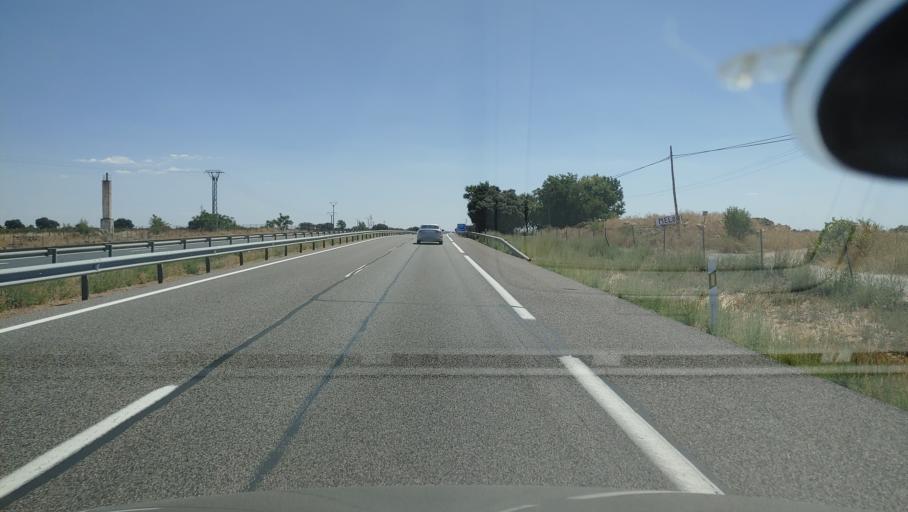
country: ES
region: Castille-La Mancha
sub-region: Provincia de Ciudad Real
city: Villarta de San Juan
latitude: 39.1979
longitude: -3.4049
